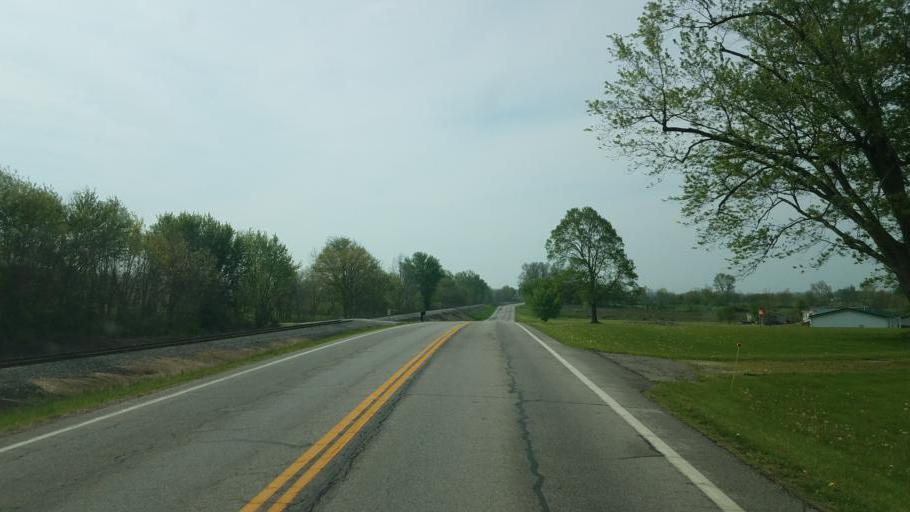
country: US
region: Ohio
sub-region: Licking County
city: Utica
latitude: 40.2899
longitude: -82.4504
